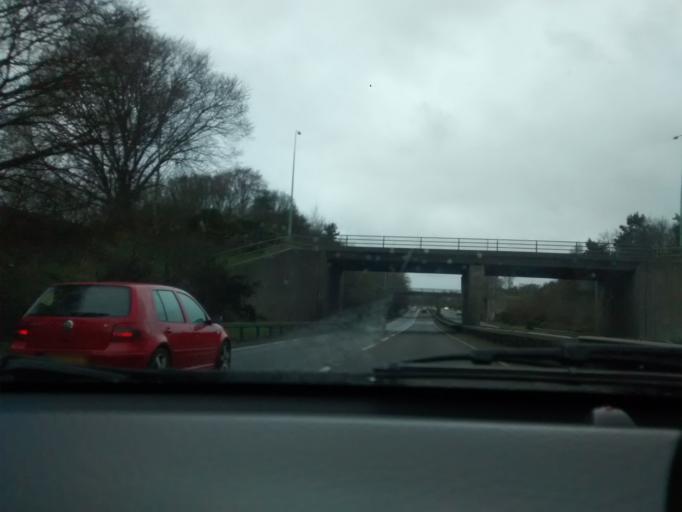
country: GB
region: England
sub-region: Suffolk
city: Felixstowe
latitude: 51.9891
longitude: 1.3191
